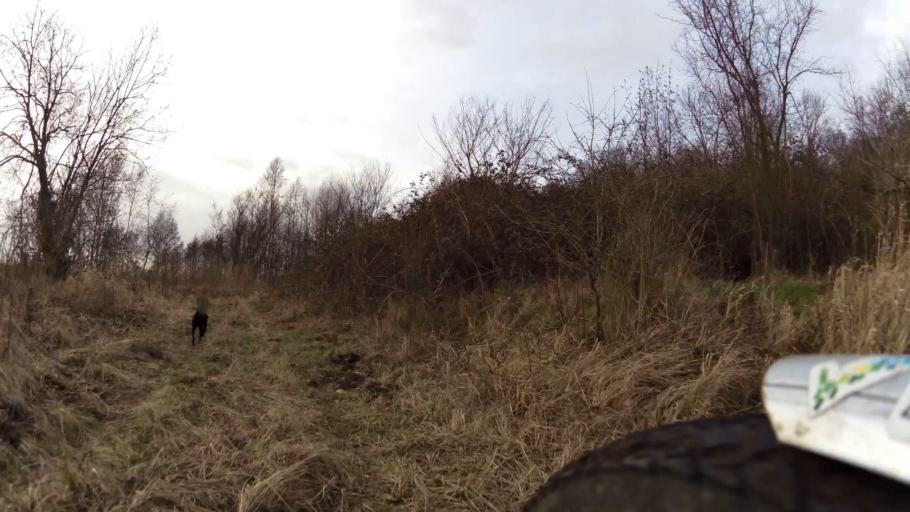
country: PL
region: West Pomeranian Voivodeship
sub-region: Powiat kamienski
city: Kamien Pomorski
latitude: 53.9334
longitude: 14.7618
